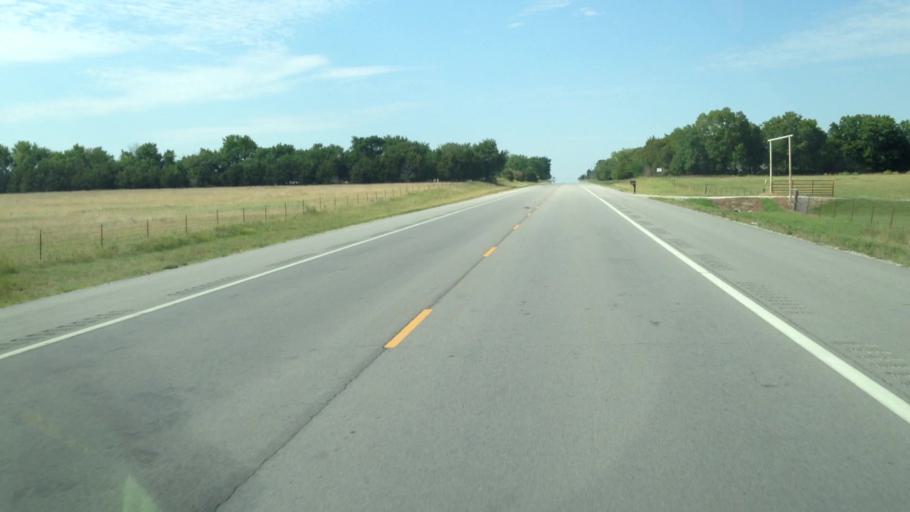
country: US
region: Kansas
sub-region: Labette County
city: Parsons
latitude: 37.3014
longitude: -95.2675
